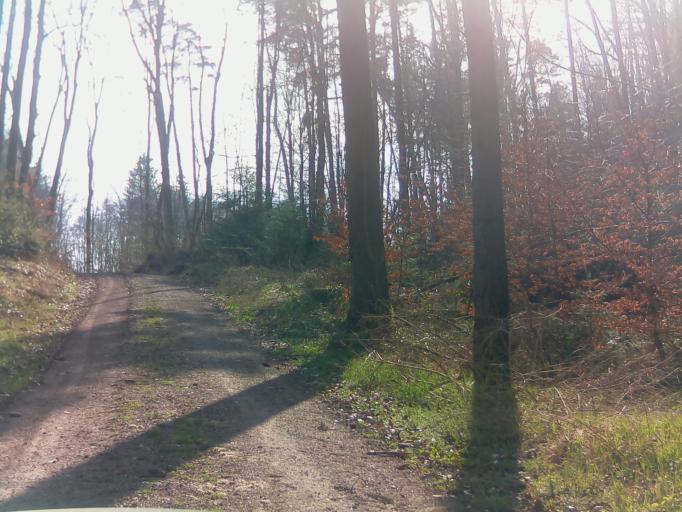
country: DE
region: Bavaria
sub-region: Swabia
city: Altenstadt
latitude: 48.1737
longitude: 10.1348
